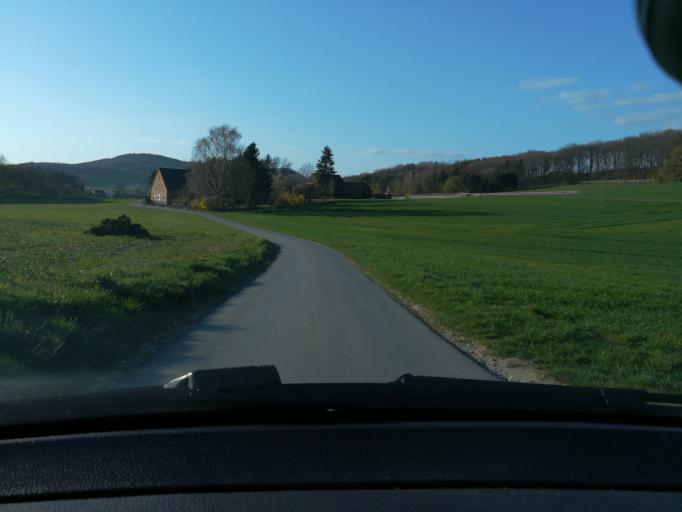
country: DE
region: North Rhine-Westphalia
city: Borgholzhausen
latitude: 52.0928
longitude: 8.3161
